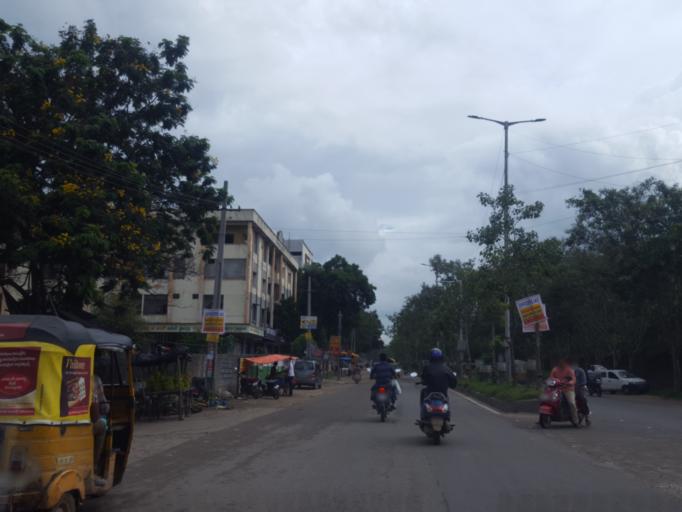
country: IN
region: Telangana
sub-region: Medak
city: Serilingampalle
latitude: 17.4907
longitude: 78.3143
